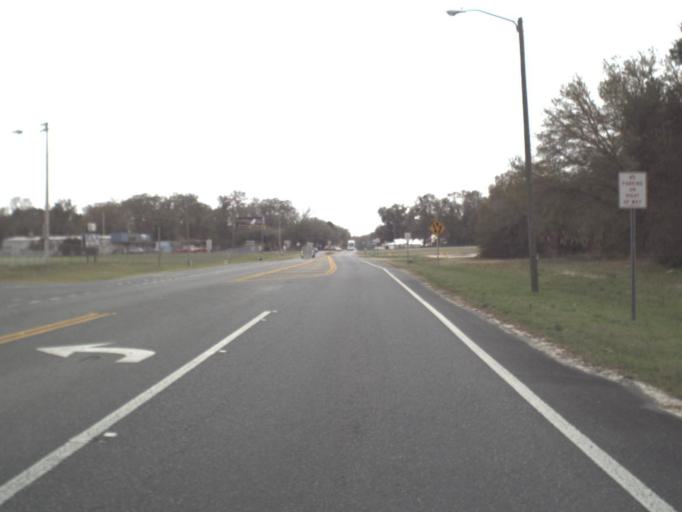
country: US
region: Florida
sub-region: Wakulla County
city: Crawfordville
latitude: 30.1074
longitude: -84.3786
